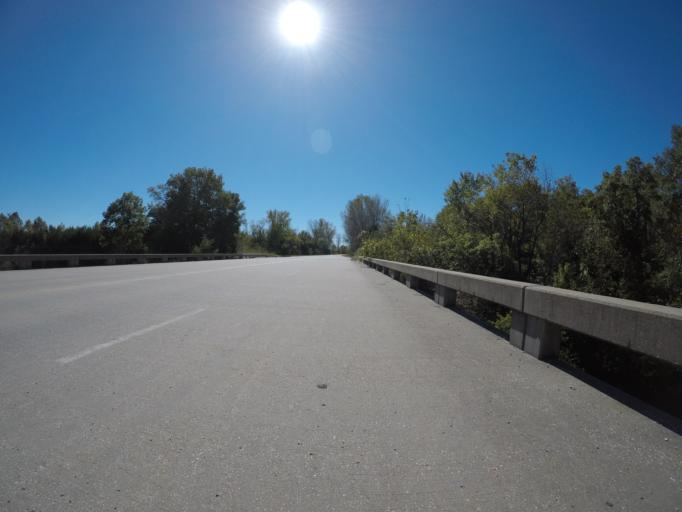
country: US
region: Kansas
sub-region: Wyandotte County
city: Bonner Springs
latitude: 39.0480
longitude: -94.8896
